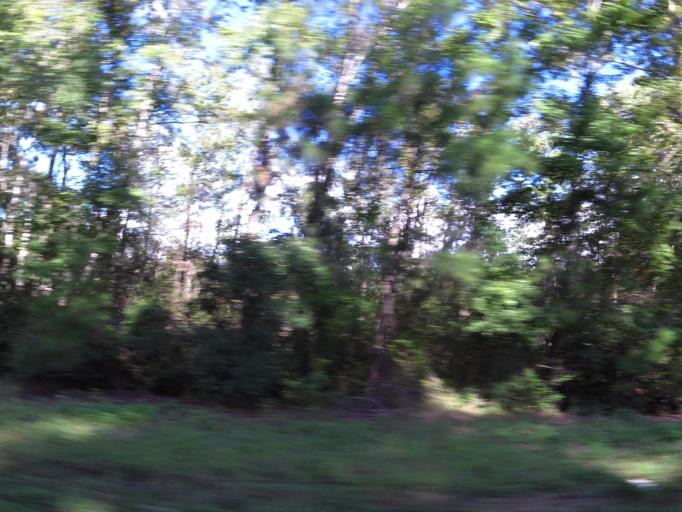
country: US
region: Georgia
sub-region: Camden County
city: Woodbine
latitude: 30.9796
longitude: -81.7272
